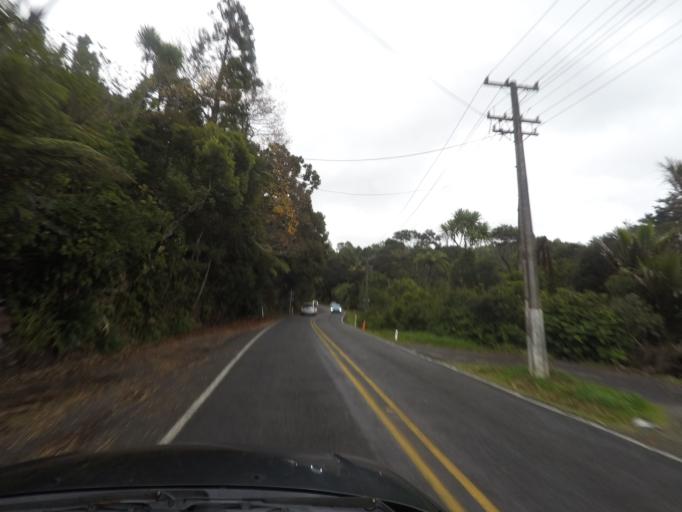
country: NZ
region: Auckland
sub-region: Auckland
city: Titirangi
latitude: -36.9310
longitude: 174.5853
